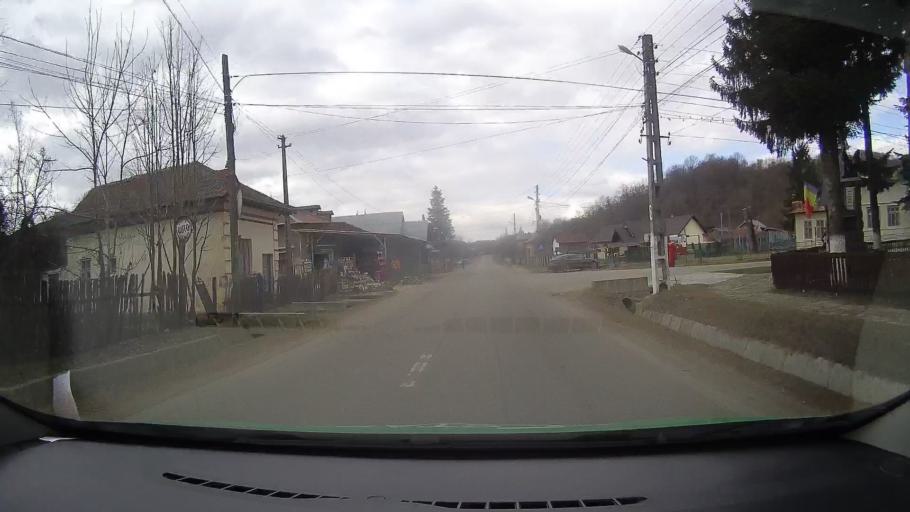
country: RO
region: Dambovita
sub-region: Comuna Valea Lunga
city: Valea Lunga-Cricov
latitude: 45.0692
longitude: 25.5780
